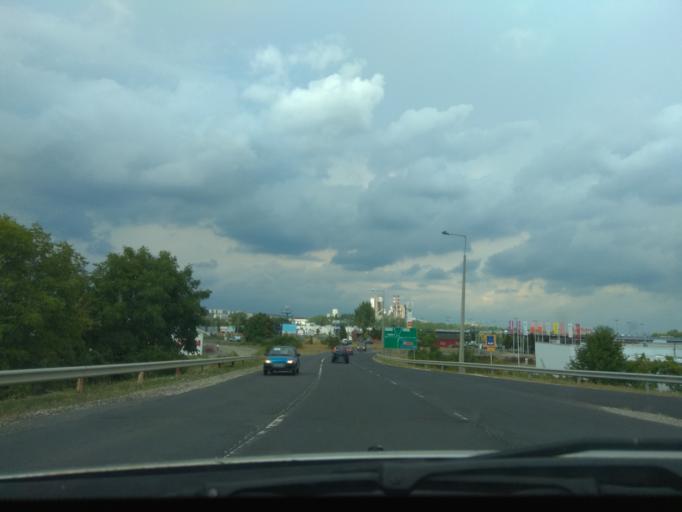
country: HU
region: Borsod-Abauj-Zemplen
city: Miskolc
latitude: 48.0535
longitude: 20.7998
